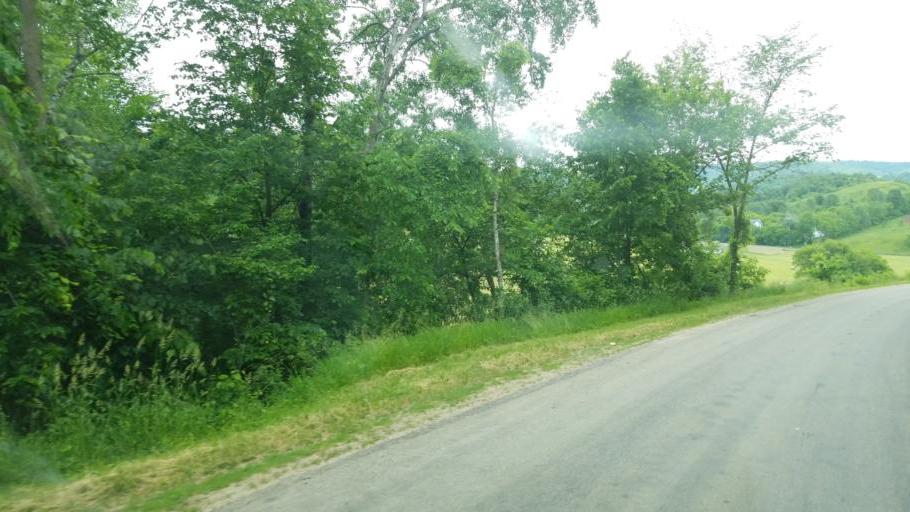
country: US
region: Wisconsin
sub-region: Monroe County
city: Cashton
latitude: 43.7149
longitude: -90.6036
